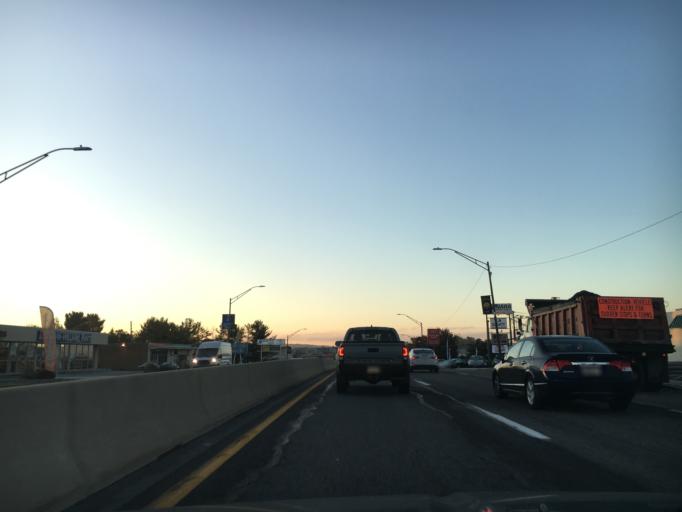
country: US
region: Pennsylvania
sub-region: Lehigh County
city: Fullerton
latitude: 40.6395
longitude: -75.4894
